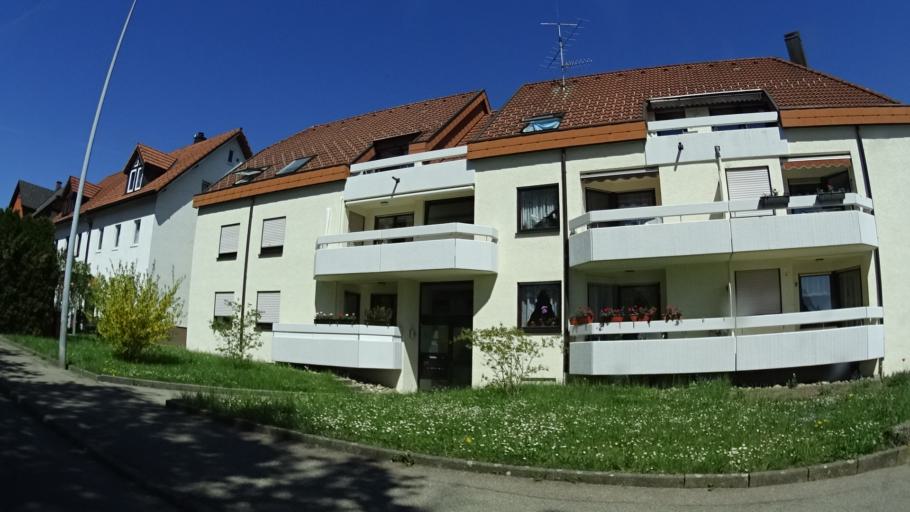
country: DE
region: Baden-Wuerttemberg
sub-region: Freiburg Region
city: Rottweil
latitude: 48.1592
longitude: 8.6388
